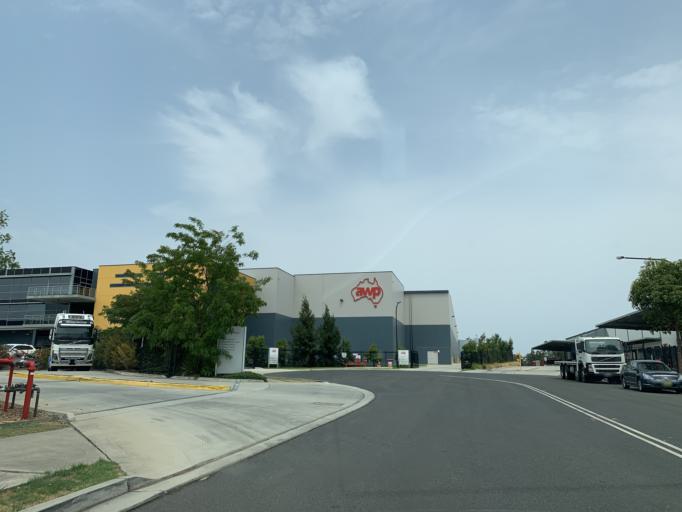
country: AU
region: New South Wales
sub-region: Blacktown
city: Blacktown
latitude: -33.8015
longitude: 150.8994
